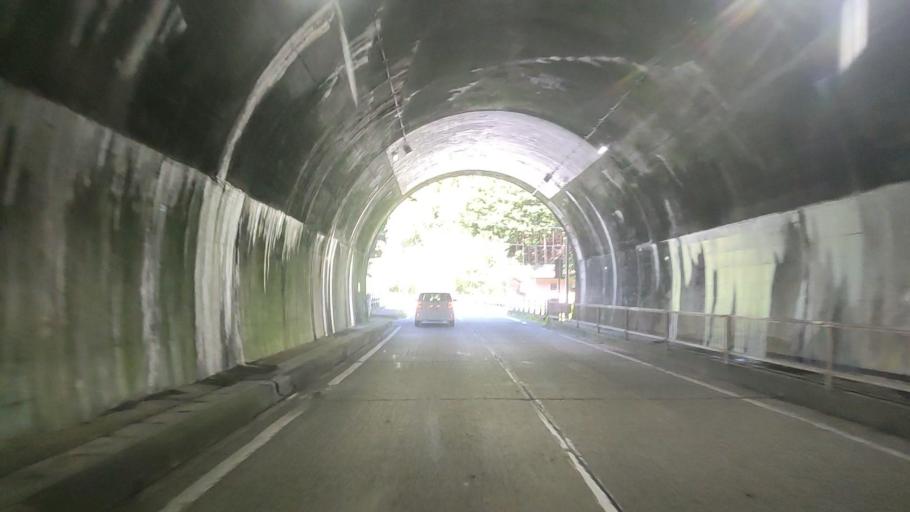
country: JP
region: Mie
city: Owase
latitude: 34.1764
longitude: 136.0035
